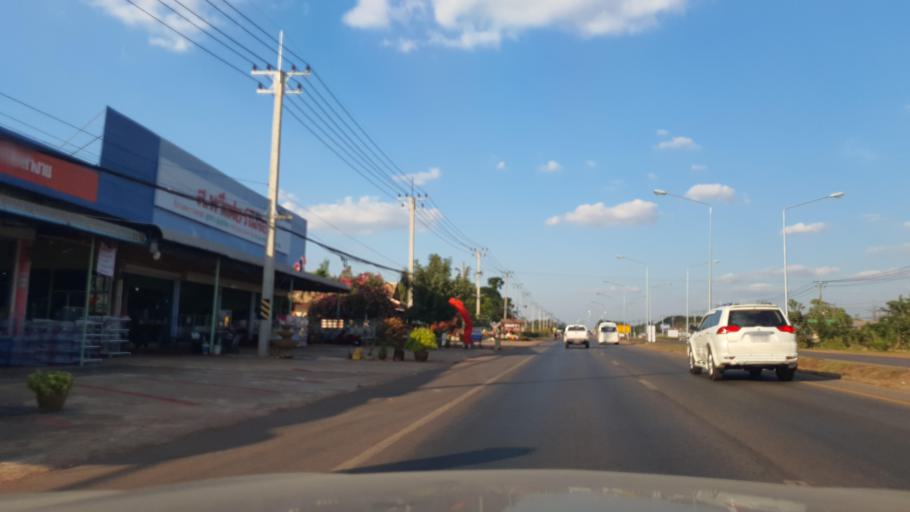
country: TH
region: Sakon Nakhon
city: Sakon Nakhon
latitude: 17.2222
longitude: 104.1052
